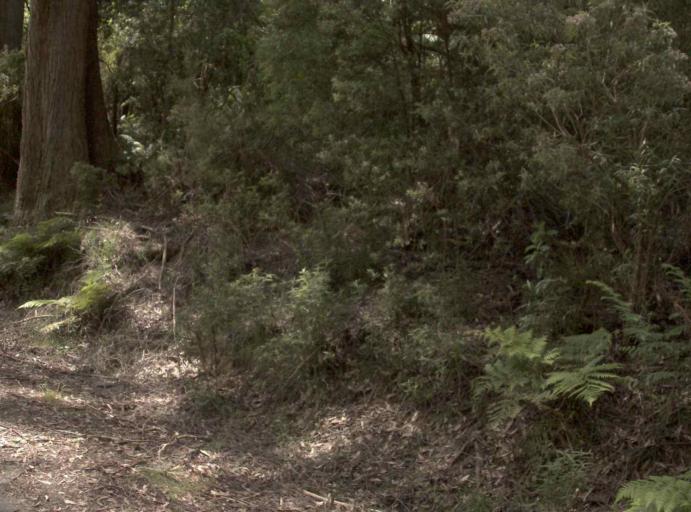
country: AU
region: Victoria
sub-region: Latrobe
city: Morwell
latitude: -38.4363
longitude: 146.5272
